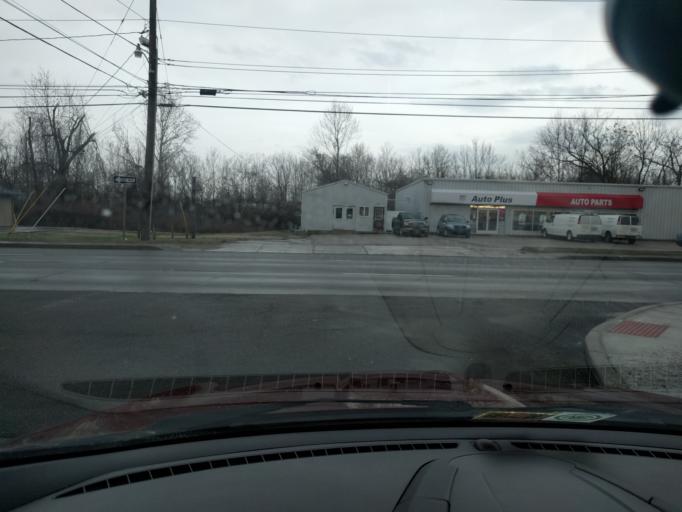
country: US
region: West Virginia
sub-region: Wood County
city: Parkersburg
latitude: 39.2749
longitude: -81.5566
